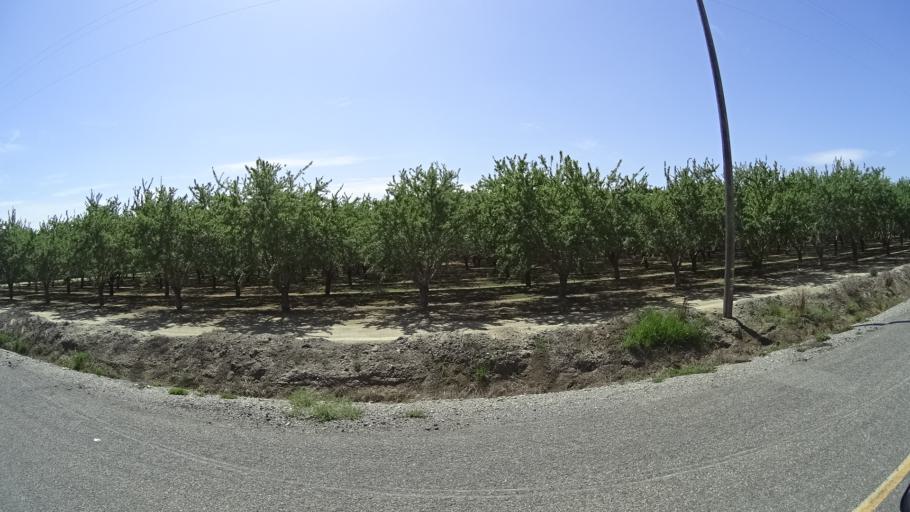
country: US
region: California
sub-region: Glenn County
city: Hamilton City
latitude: 39.6524
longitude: -122.0680
